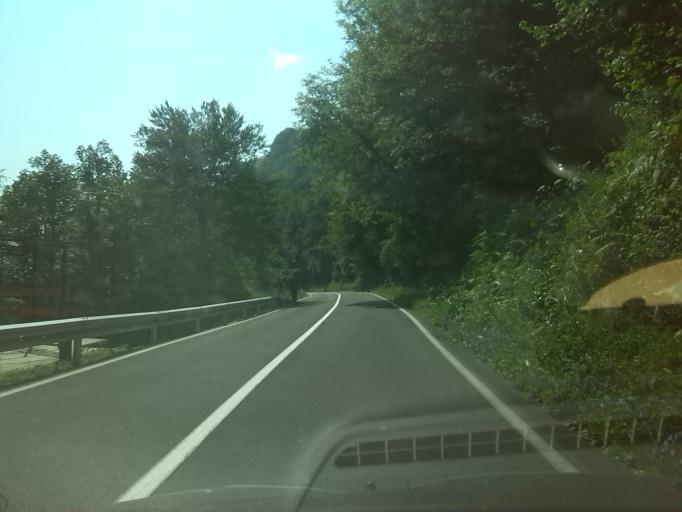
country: IT
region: Friuli Venezia Giulia
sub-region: Provincia di Udine
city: Cras
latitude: 46.2148
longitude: 13.6131
